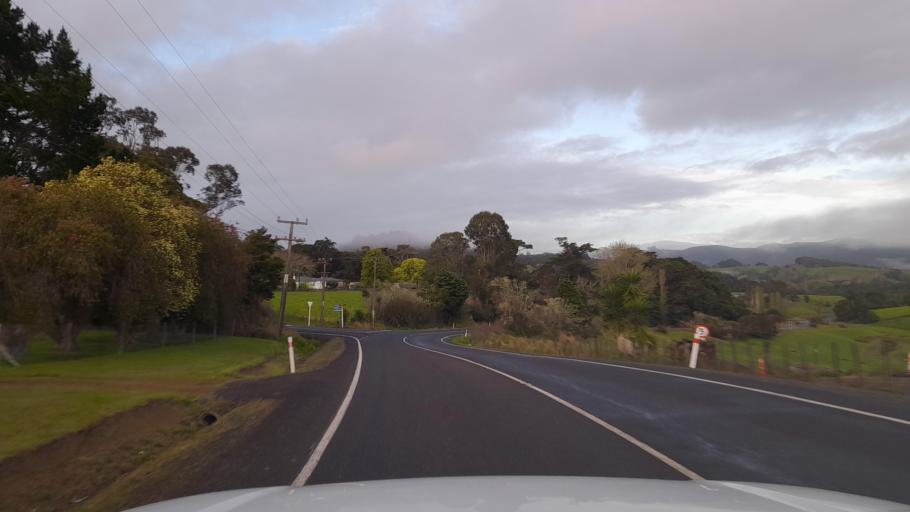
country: NZ
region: Northland
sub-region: Kaipara District
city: Dargaville
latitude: -35.7140
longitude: 173.9544
